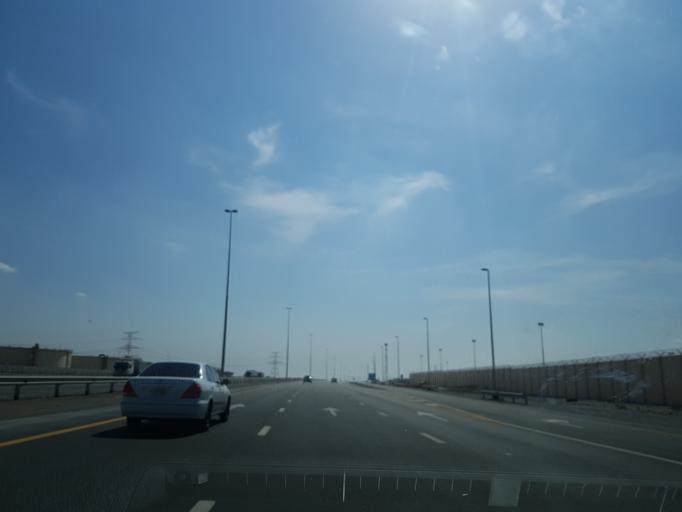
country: AE
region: Ra's al Khaymah
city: Ras al-Khaimah
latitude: 25.7758
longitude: 56.0292
